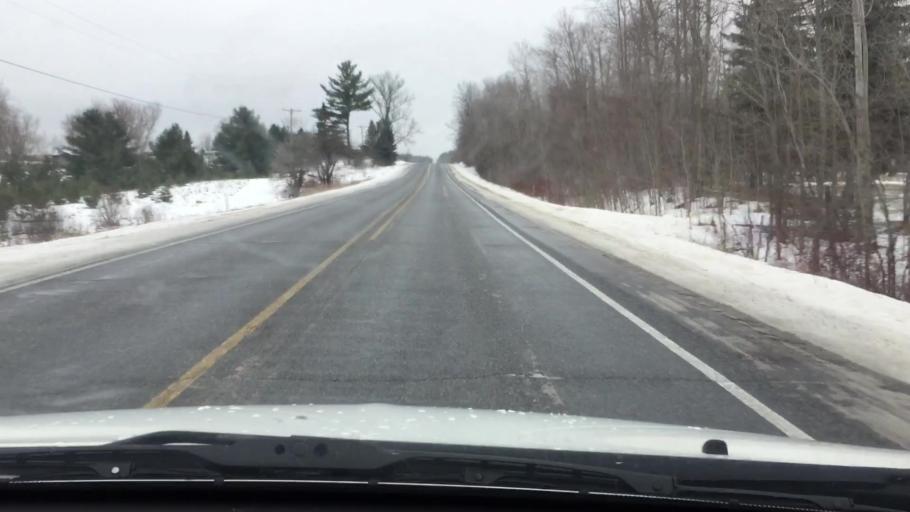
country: US
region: Michigan
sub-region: Wexford County
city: Cadillac
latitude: 44.1117
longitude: -85.4443
